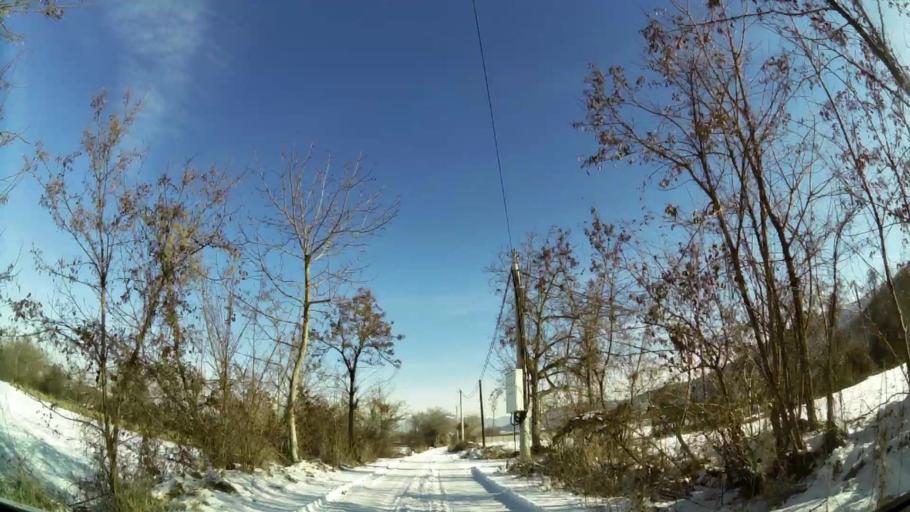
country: MK
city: Grchec
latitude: 41.9825
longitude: 21.3241
